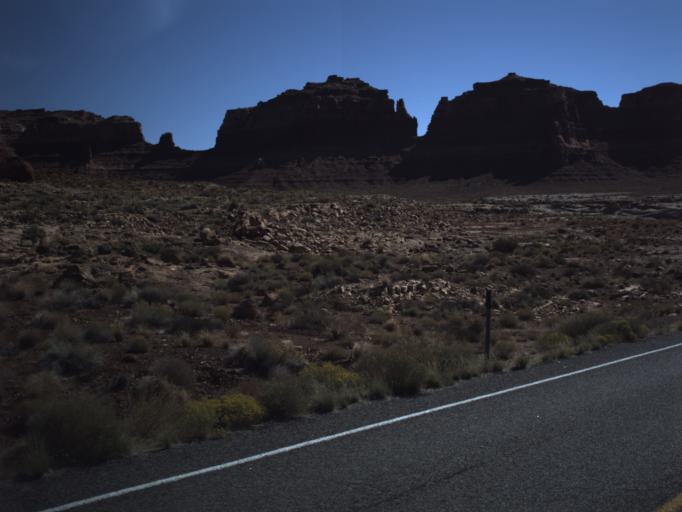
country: US
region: Utah
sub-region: San Juan County
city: Blanding
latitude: 37.9063
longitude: -110.3817
